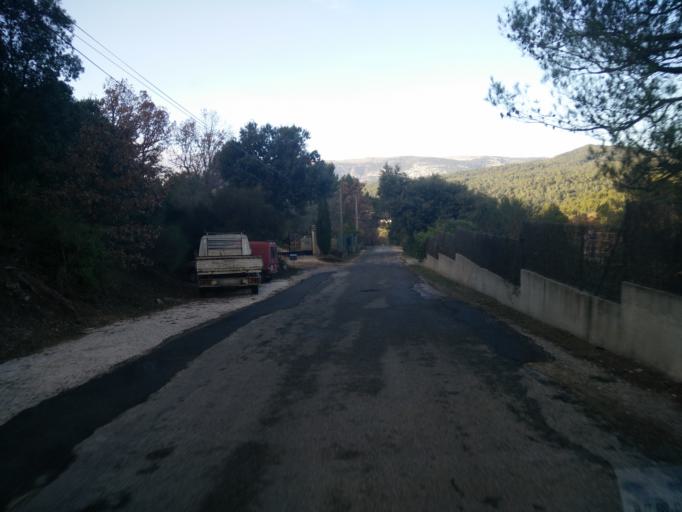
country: FR
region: Provence-Alpes-Cote d'Azur
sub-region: Departement du Var
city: Signes
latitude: 43.2769
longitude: 5.8465
